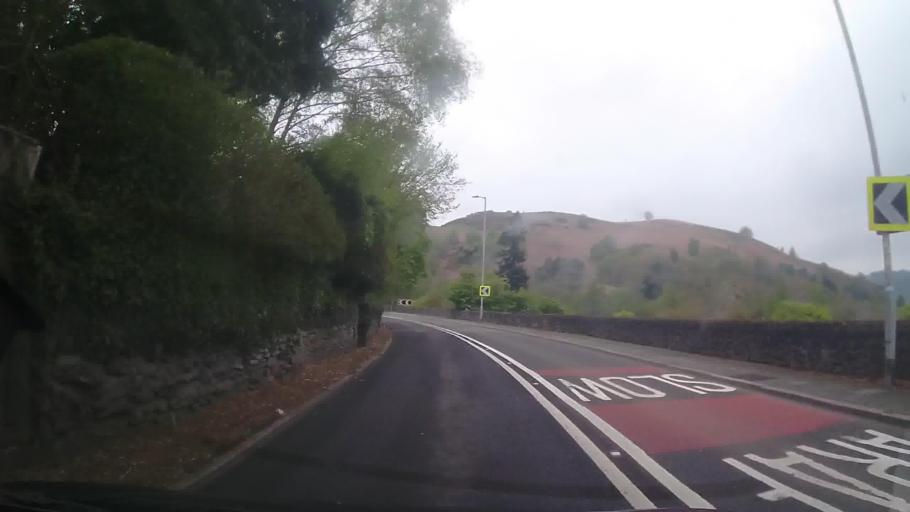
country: GB
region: Wales
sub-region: Denbighshire
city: Llangollen
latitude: 52.9836
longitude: -3.1859
